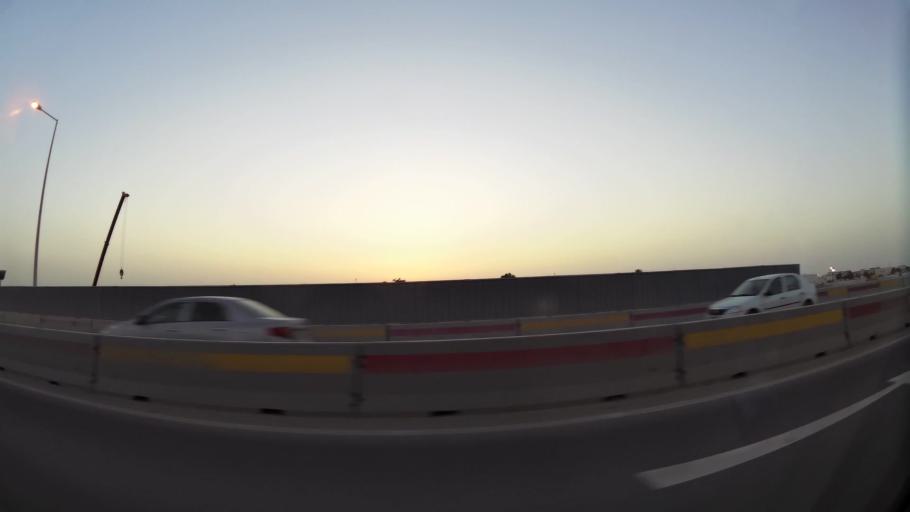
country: QA
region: Baladiyat ar Rayyan
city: Ar Rayyan
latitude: 25.3012
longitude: 51.4650
